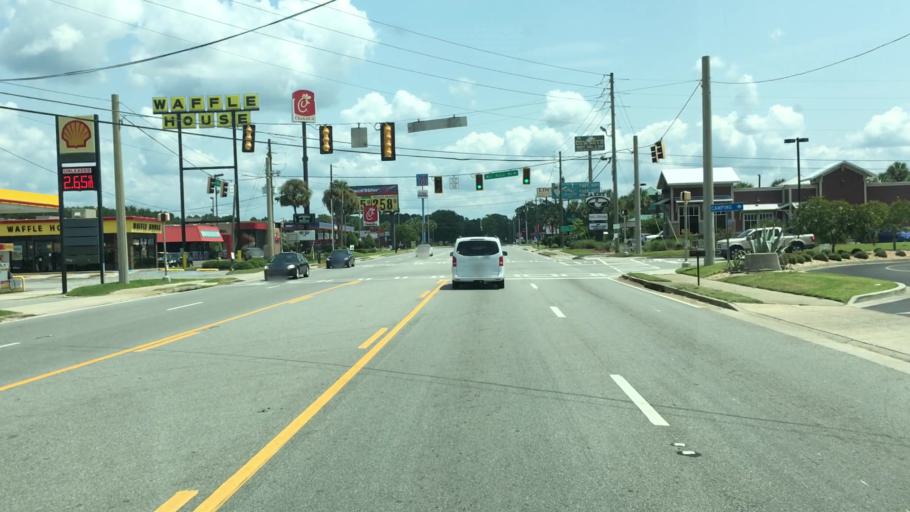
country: US
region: Georgia
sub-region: Lowndes County
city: Valdosta
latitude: 30.6810
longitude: -83.2209
